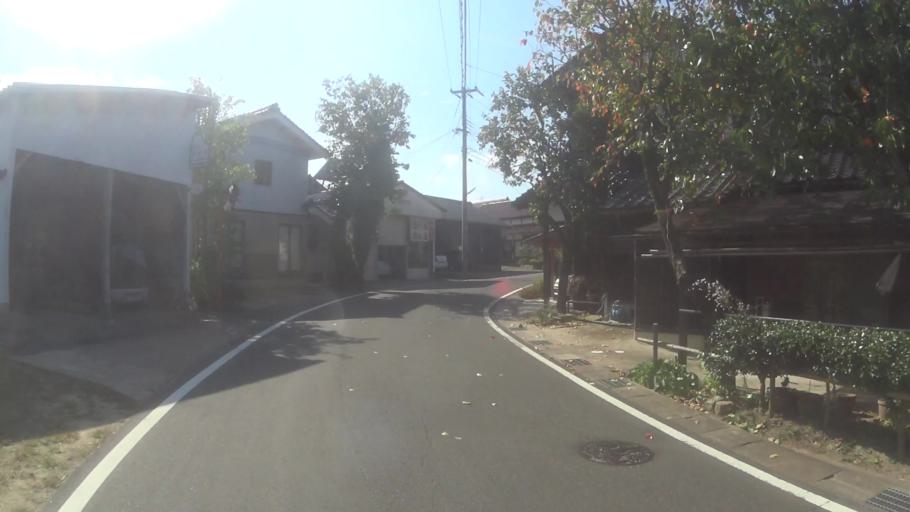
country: JP
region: Kyoto
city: Miyazu
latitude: 35.6801
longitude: 135.1032
